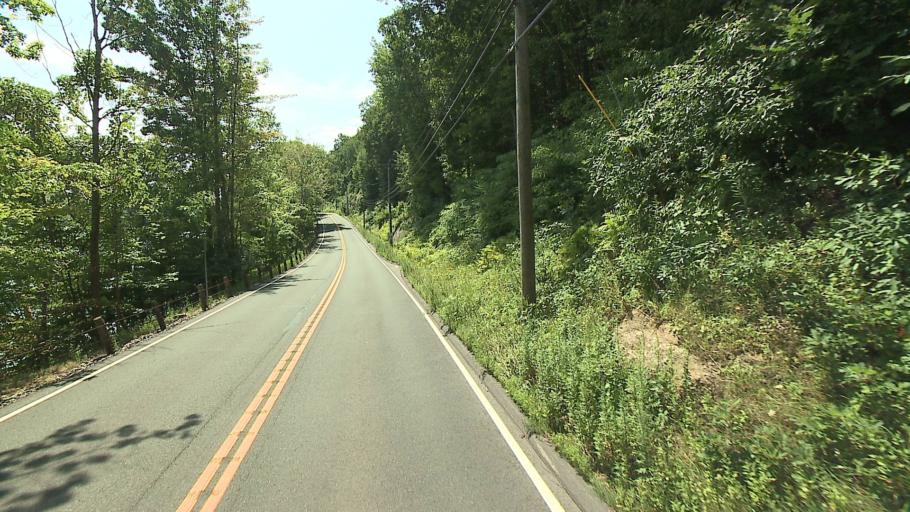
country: US
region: New York
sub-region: Putnam County
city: Putnam Lake
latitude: 41.4953
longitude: -73.4690
